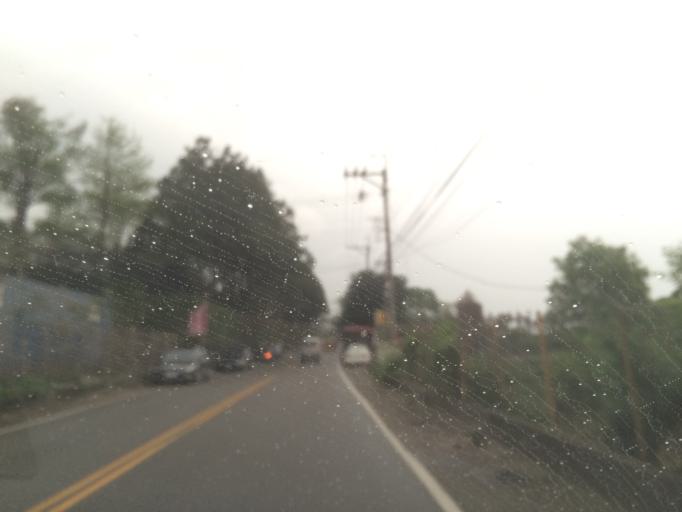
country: TW
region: Taiwan
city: Fengyuan
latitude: 24.1870
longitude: 120.8145
